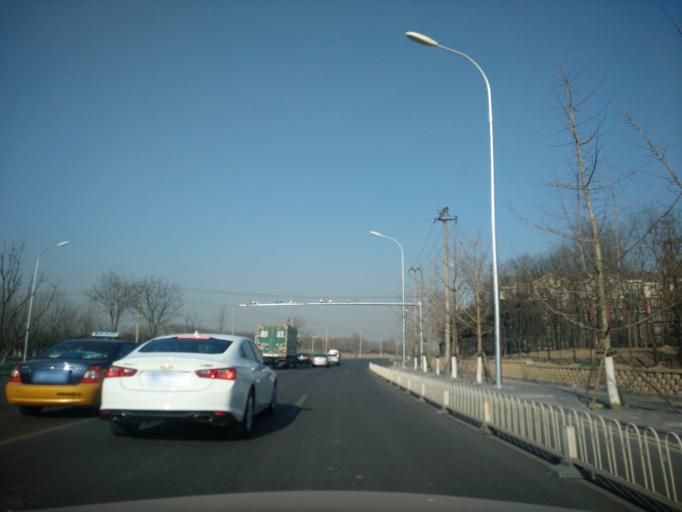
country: CN
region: Beijing
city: Jiugong
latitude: 39.8150
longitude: 116.5097
